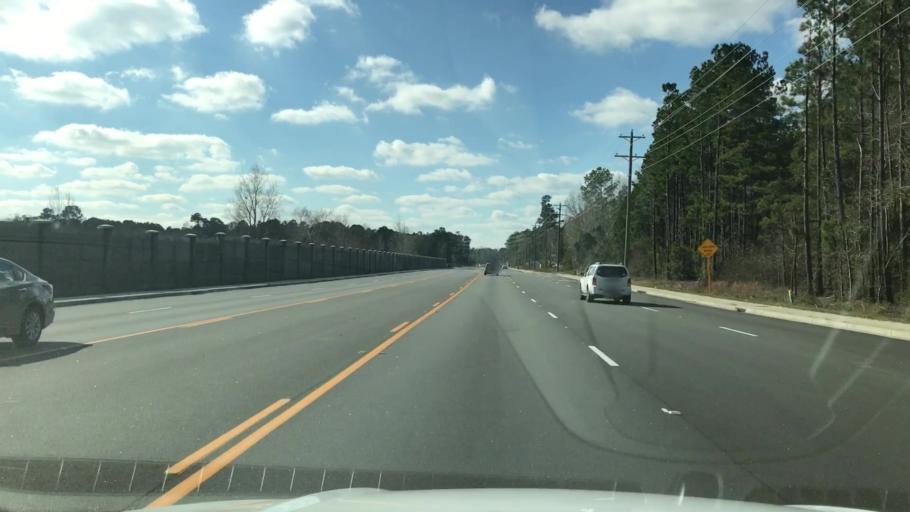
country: US
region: South Carolina
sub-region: Horry County
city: Socastee
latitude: 33.6463
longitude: -79.0256
